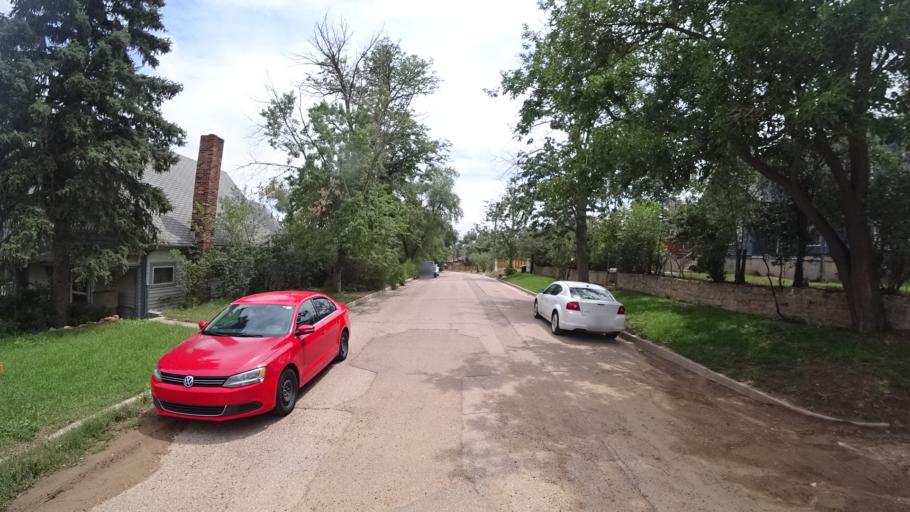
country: US
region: Colorado
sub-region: El Paso County
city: Colorado Springs
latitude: 38.8493
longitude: -104.8348
